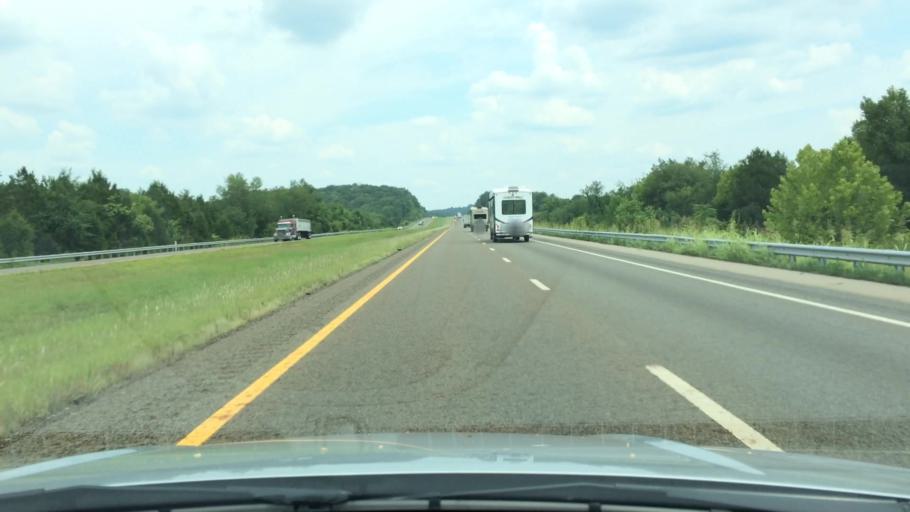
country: US
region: Tennessee
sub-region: Maury County
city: Columbia
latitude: 35.6013
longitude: -86.9015
